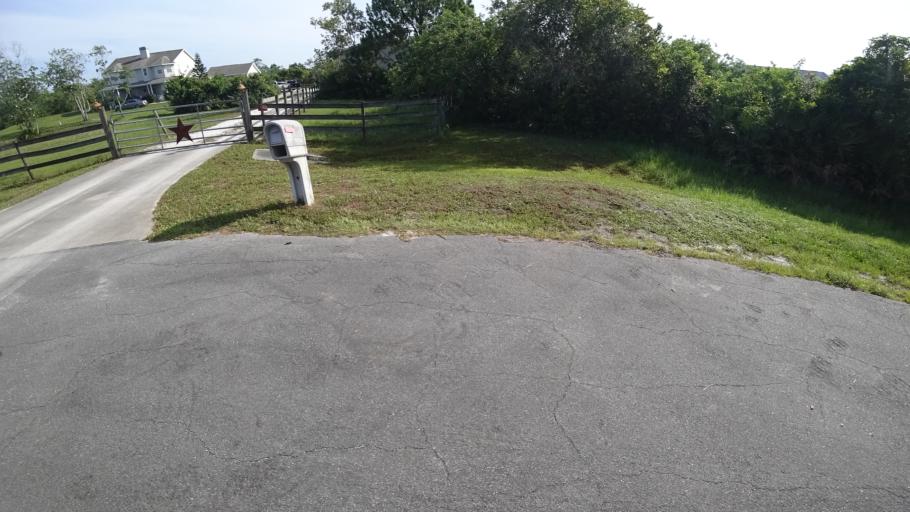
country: US
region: Florida
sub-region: Sarasota County
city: Lake Sarasota
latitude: 27.3600
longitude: -82.2485
